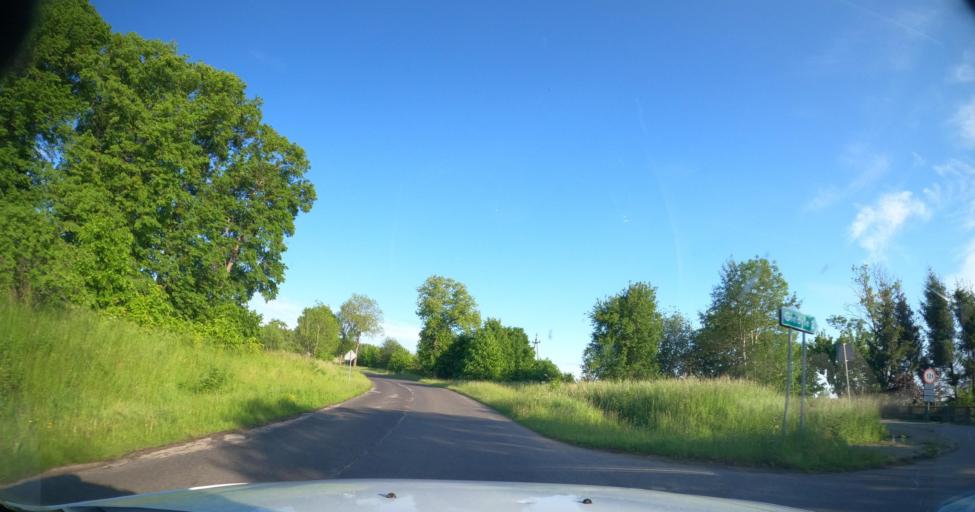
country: PL
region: Warmian-Masurian Voivodeship
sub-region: Powiat braniewski
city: Braniewo
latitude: 54.2686
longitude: 19.9386
